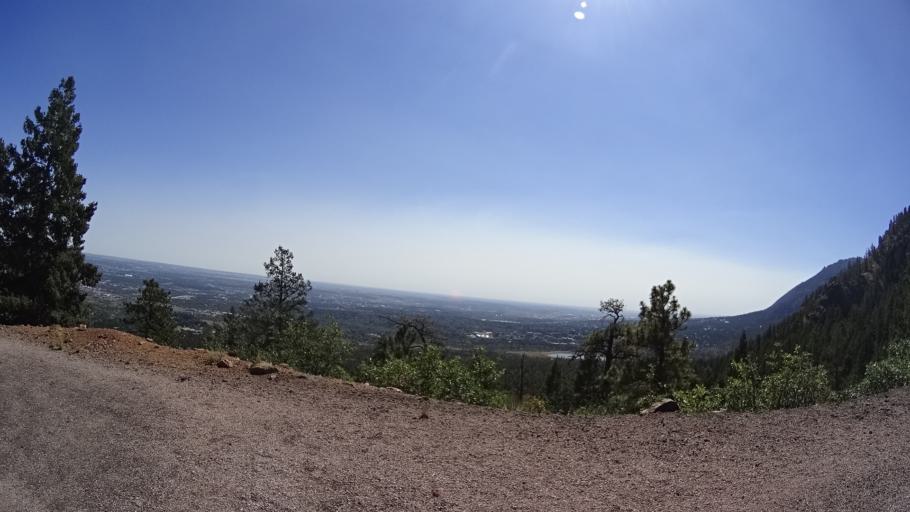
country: US
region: Colorado
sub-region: El Paso County
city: Colorado Springs
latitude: 38.8047
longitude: -104.8793
